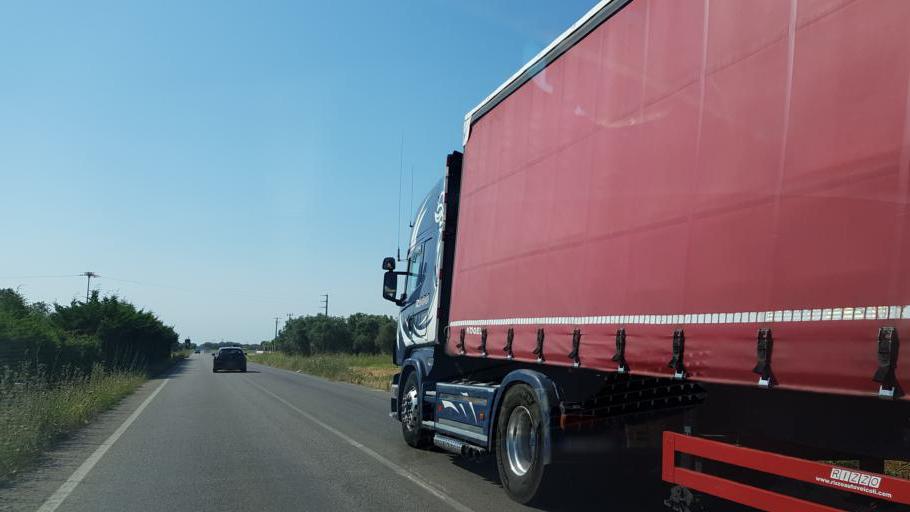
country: IT
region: Apulia
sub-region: Provincia di Lecce
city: Guagnano
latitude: 40.4111
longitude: 17.9608
